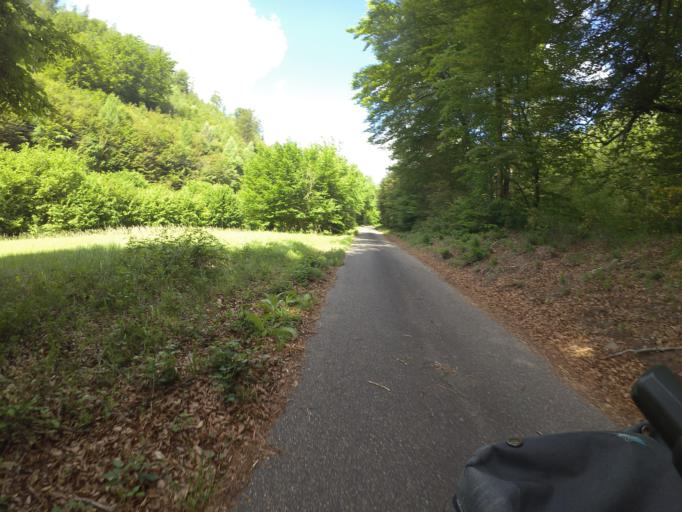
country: DE
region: Rheinland-Pfalz
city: Fischbach
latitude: 49.1147
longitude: 7.6930
